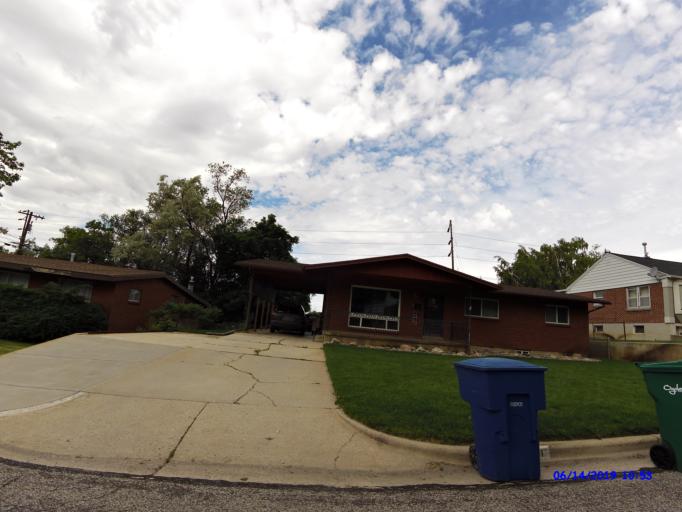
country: US
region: Utah
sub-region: Weber County
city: Ogden
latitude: 41.2470
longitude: -111.9474
